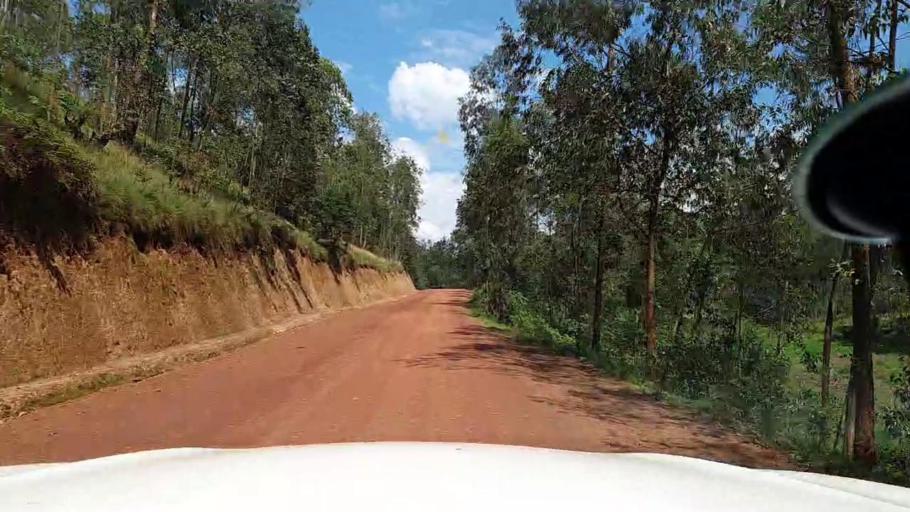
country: RW
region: Northern Province
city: Byumba
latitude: -1.7575
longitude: 29.8692
